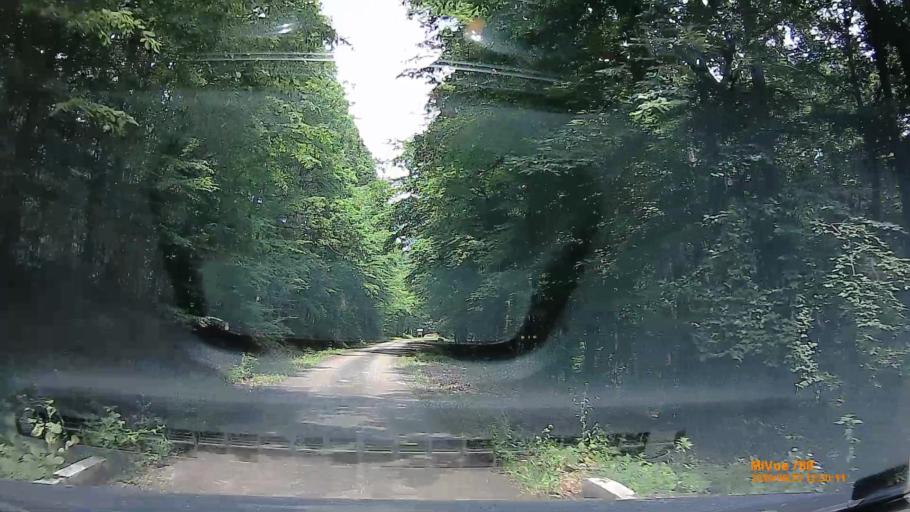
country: HU
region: Baranya
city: Hosszuheteny
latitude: 46.2131
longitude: 18.3507
